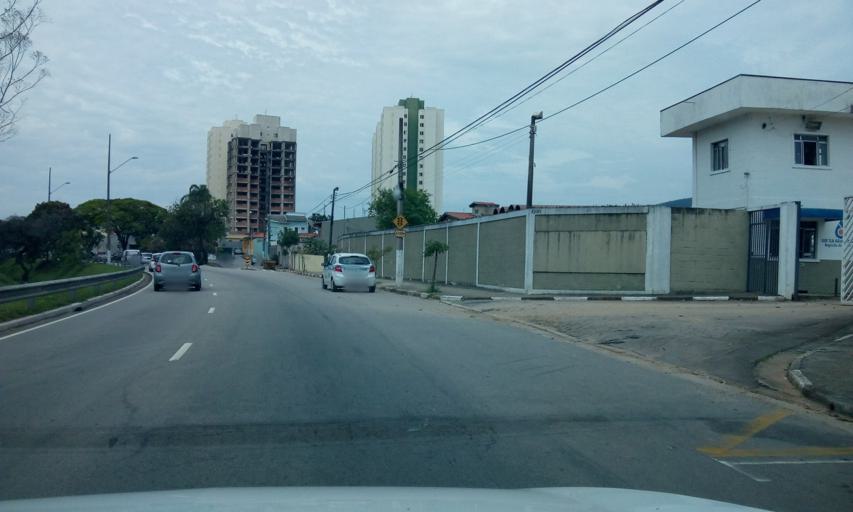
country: BR
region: Sao Paulo
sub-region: Jundiai
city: Jundiai
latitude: -23.2159
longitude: -46.8752
